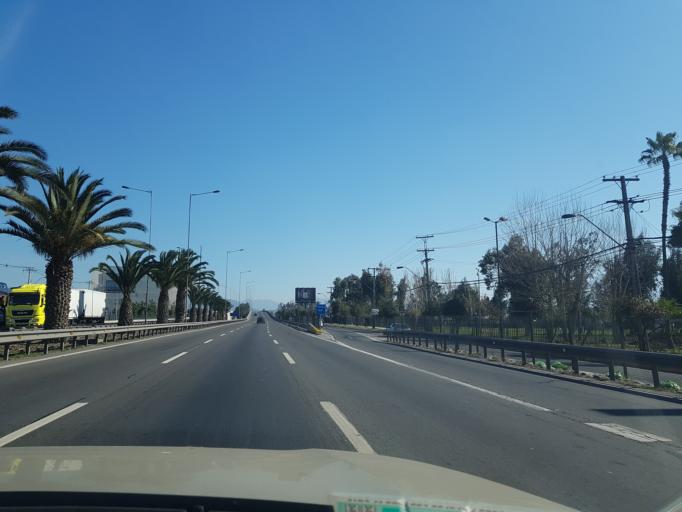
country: CL
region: Santiago Metropolitan
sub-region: Provincia de Santiago
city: Lo Prado
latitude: -33.3911
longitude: -70.7657
